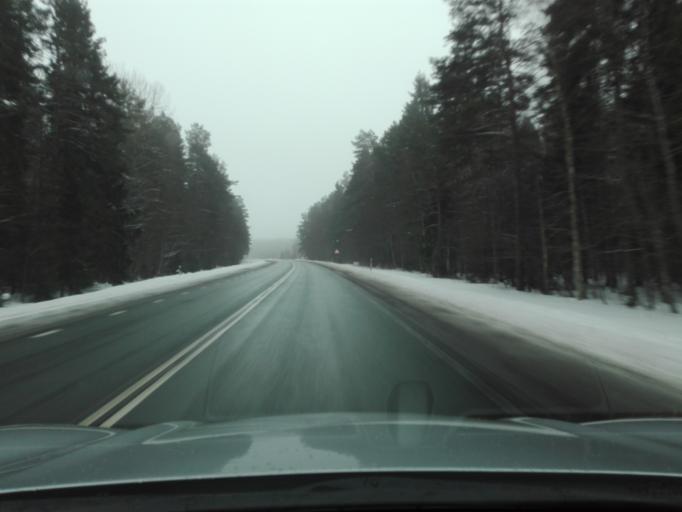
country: EE
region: Raplamaa
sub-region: Kohila vald
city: Kohila
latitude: 59.1658
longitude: 24.7714
